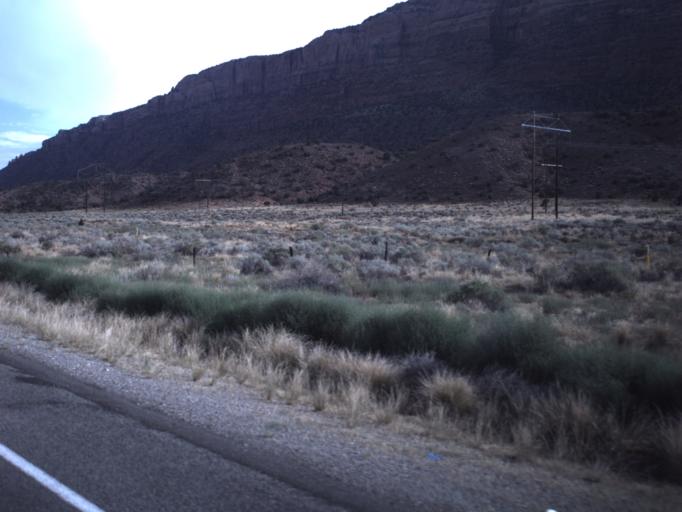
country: US
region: Utah
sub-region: Grand County
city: Moab
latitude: 38.4929
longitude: -109.4685
